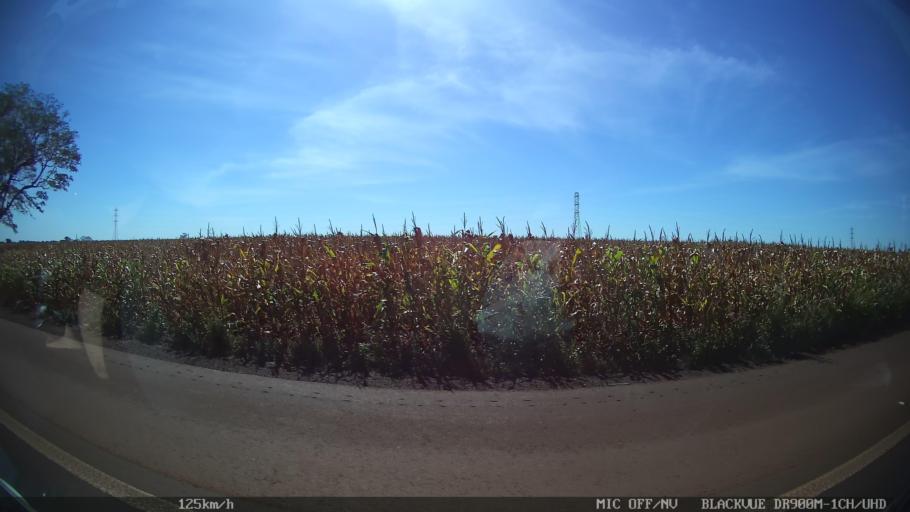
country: BR
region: Sao Paulo
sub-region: Guaira
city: Guaira
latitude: -20.4444
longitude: -48.3690
